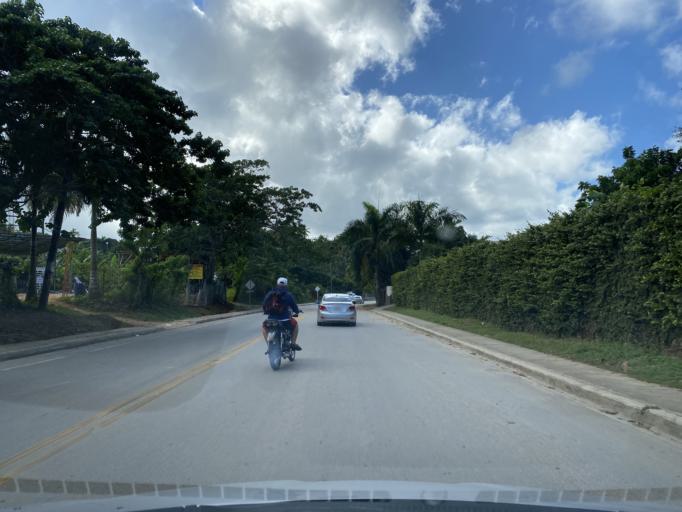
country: DO
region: Samana
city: Las Terrenas
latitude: 19.3055
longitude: -69.5420
